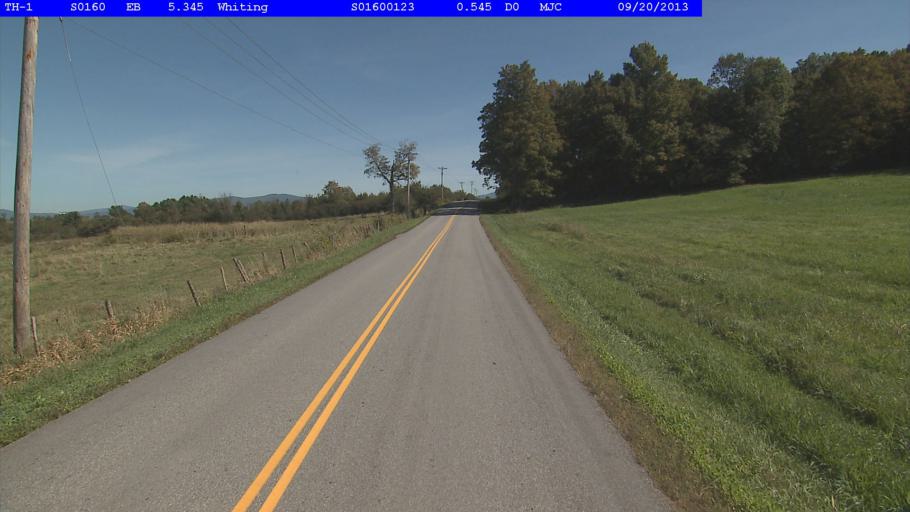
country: US
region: Vermont
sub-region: Rutland County
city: Brandon
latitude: 43.8628
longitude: -73.2147
